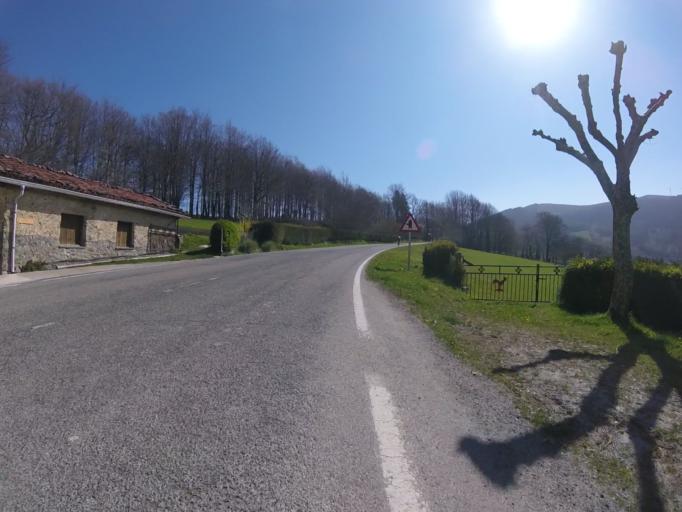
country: ES
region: Navarre
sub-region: Provincia de Navarra
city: Leitza
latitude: 43.0863
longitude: -1.8836
